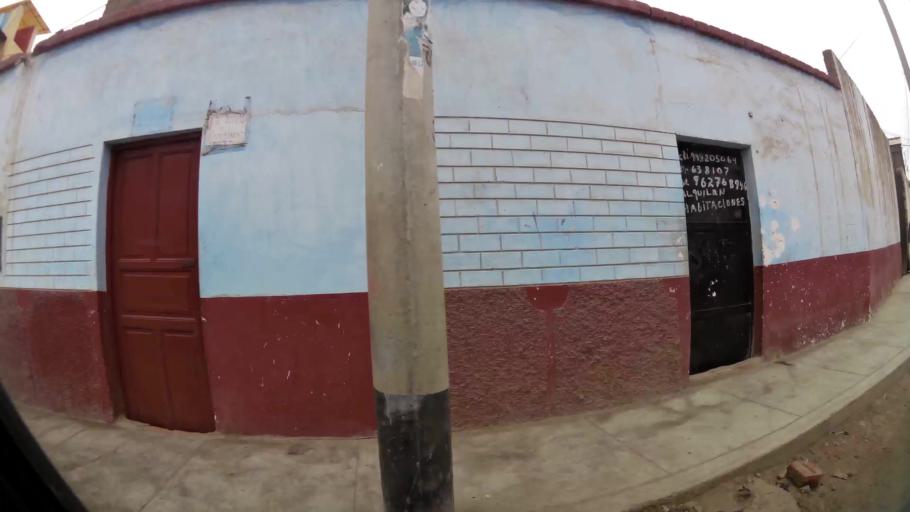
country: PE
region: La Libertad
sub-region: Provincia de Trujillo
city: La Esperanza
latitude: -8.0993
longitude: -79.0459
